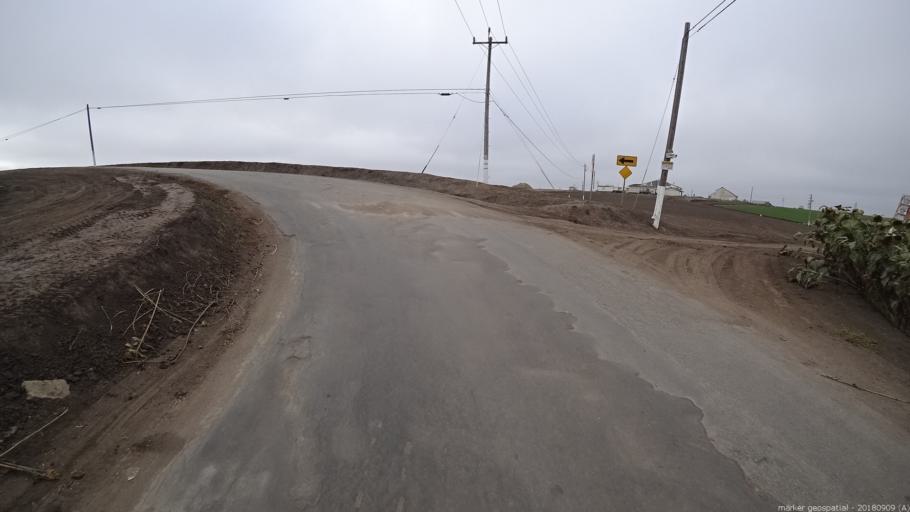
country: US
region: California
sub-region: Monterey County
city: Boronda
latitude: 36.7071
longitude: -121.6789
